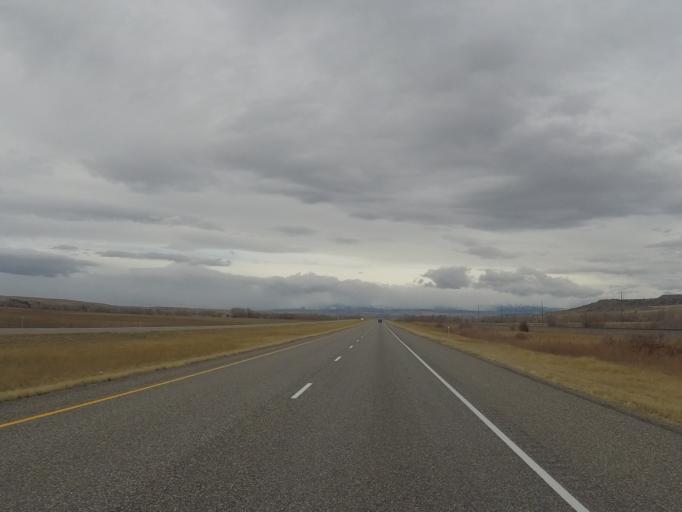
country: US
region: Montana
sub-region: Sweet Grass County
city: Big Timber
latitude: 45.7839
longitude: -109.8129
